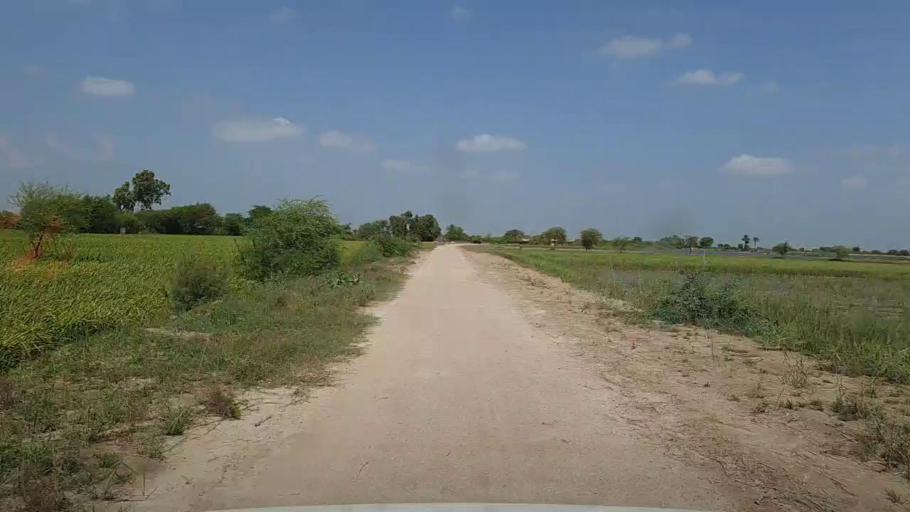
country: PK
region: Sindh
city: Kario
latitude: 24.6915
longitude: 68.5880
